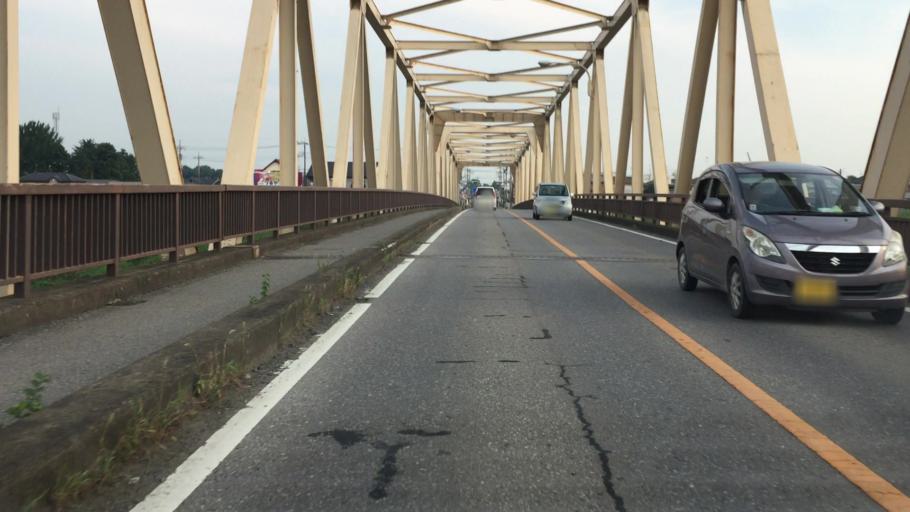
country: JP
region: Tochigi
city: Fujioka
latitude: 36.2652
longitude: 139.6501
